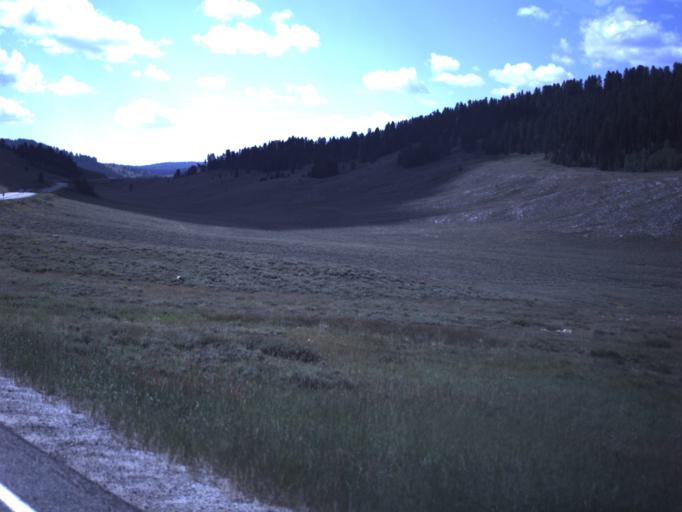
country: US
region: Idaho
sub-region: Bear Lake County
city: Paris
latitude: 41.9489
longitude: -111.4822
